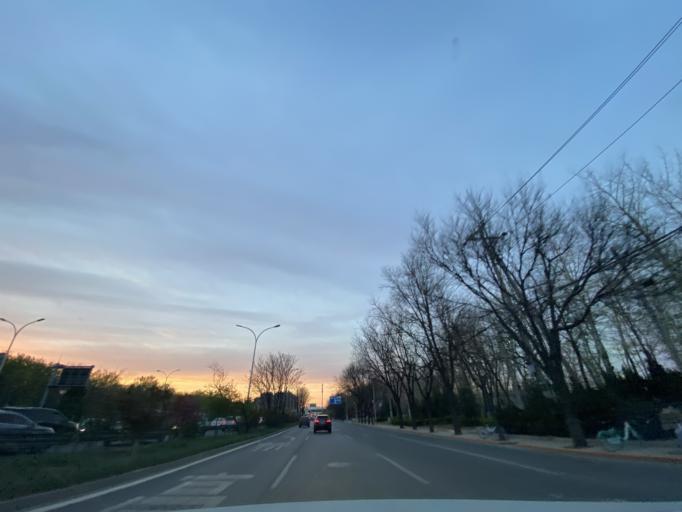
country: CN
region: Beijing
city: Qinghe
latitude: 40.0170
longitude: 116.3513
